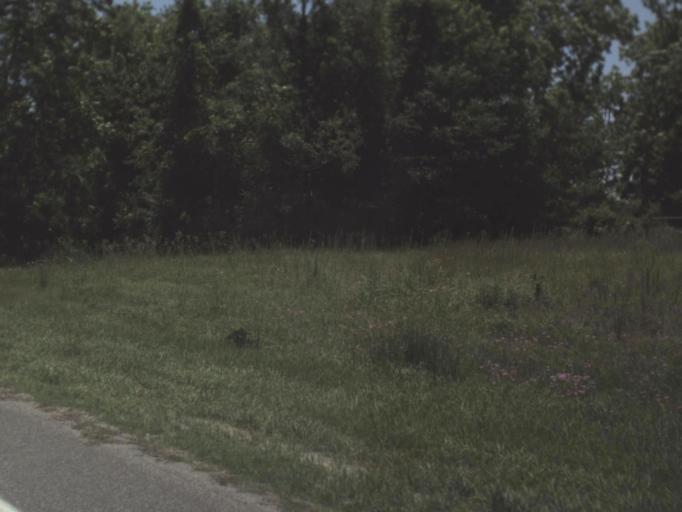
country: US
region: Florida
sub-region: Suwannee County
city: Live Oak
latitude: 30.3403
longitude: -83.0832
